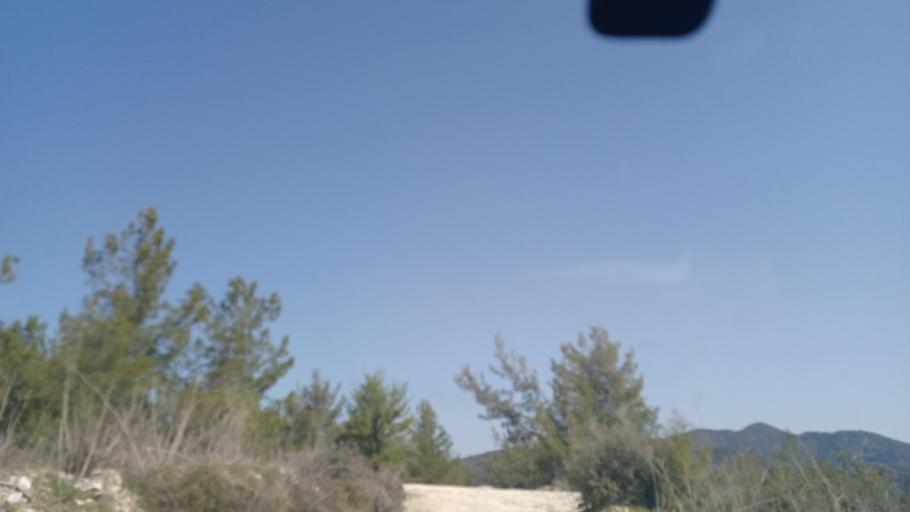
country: CY
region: Limassol
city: Pachna
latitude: 34.8828
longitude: 32.7328
